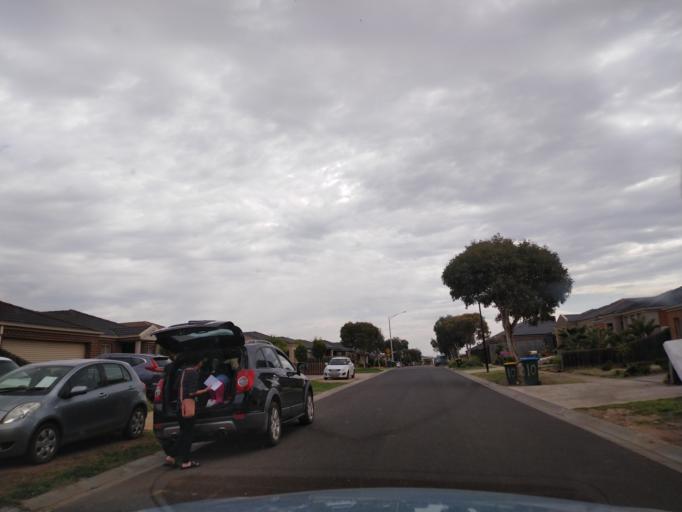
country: AU
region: Victoria
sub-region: Wyndham
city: Williams Landing
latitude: -37.8430
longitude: 144.7175
